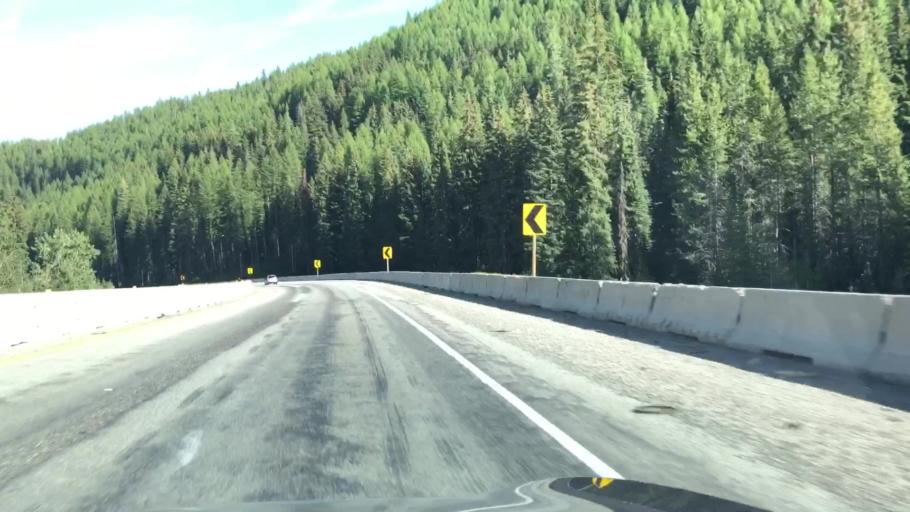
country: US
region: Idaho
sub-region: Shoshone County
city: Wallace
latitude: 47.4341
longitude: -115.6723
